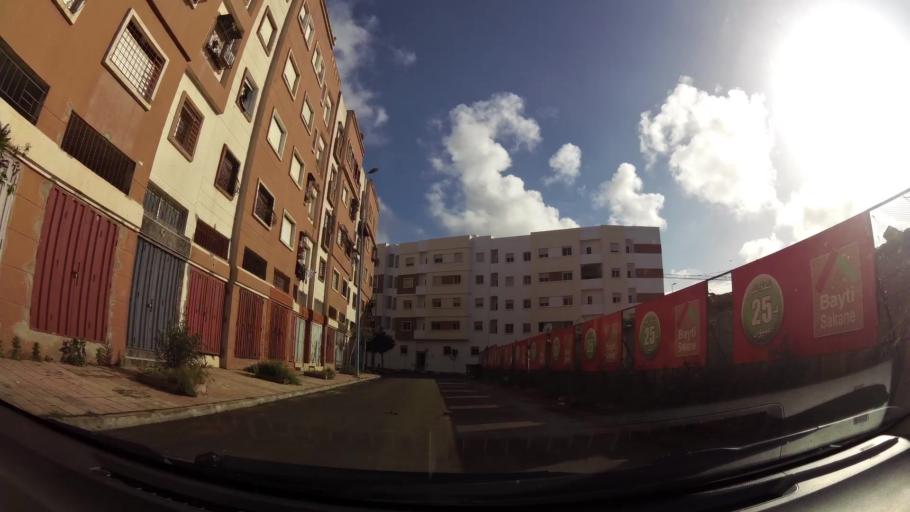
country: MA
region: Grand Casablanca
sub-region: Casablanca
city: Casablanca
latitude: 33.5563
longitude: -7.7053
